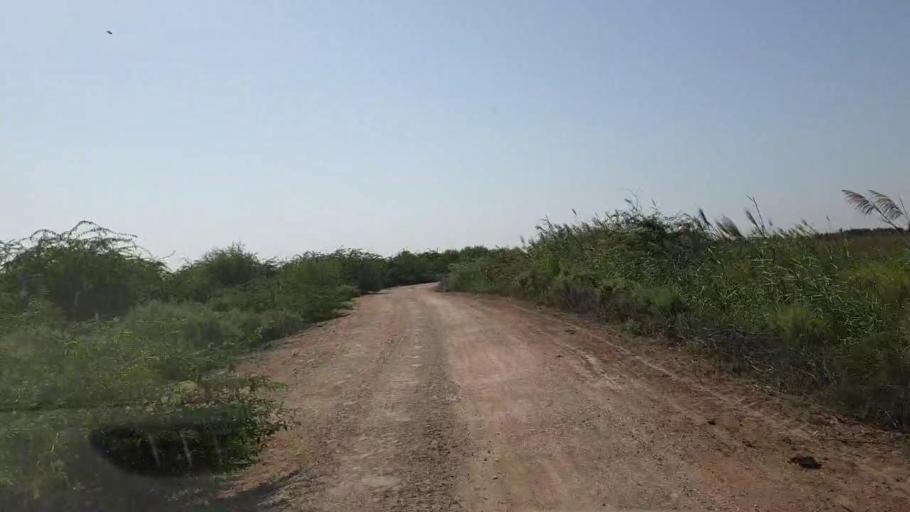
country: PK
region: Sindh
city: Tando Bago
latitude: 24.7065
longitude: 69.0443
